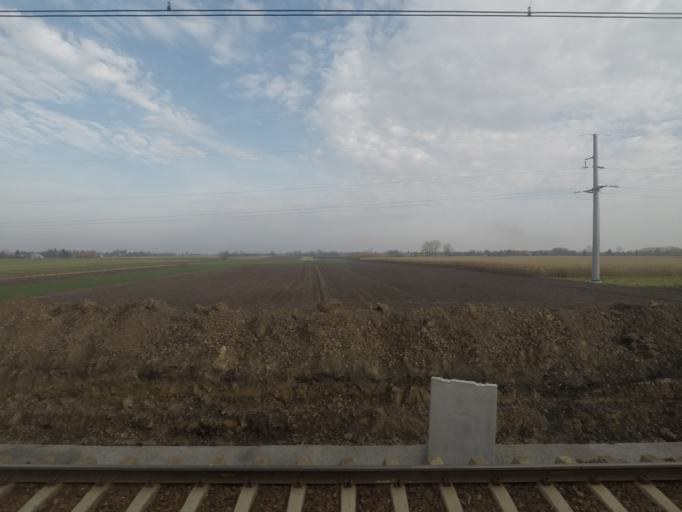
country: PL
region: Subcarpathian Voivodeship
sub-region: Powiat jaroslawski
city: Sosnica
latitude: 49.9018
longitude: 22.8515
